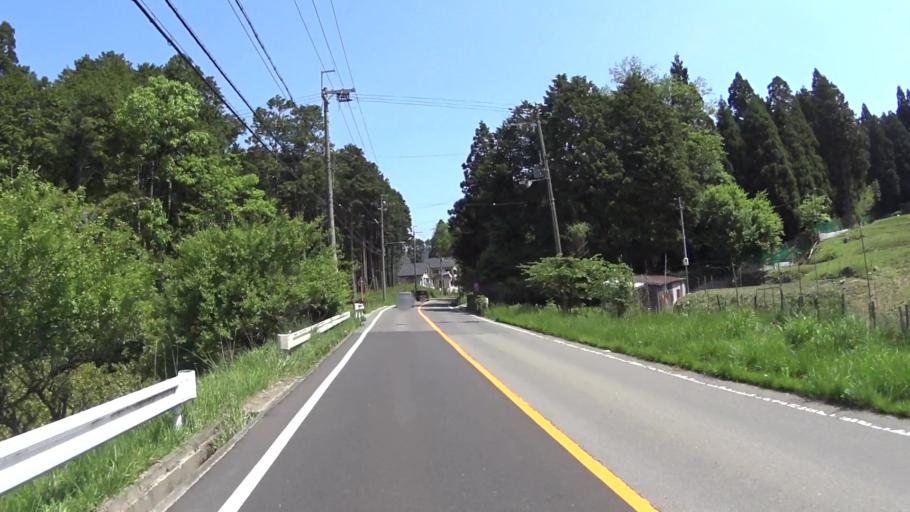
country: JP
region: Shiga Prefecture
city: Kitahama
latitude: 35.1330
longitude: 135.8340
